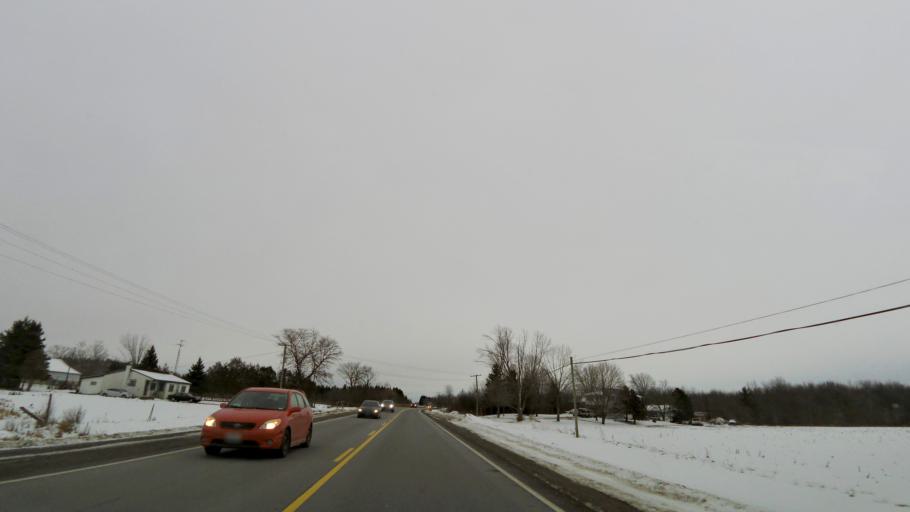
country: CA
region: Ontario
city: Cambridge
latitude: 43.3101
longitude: -80.1546
